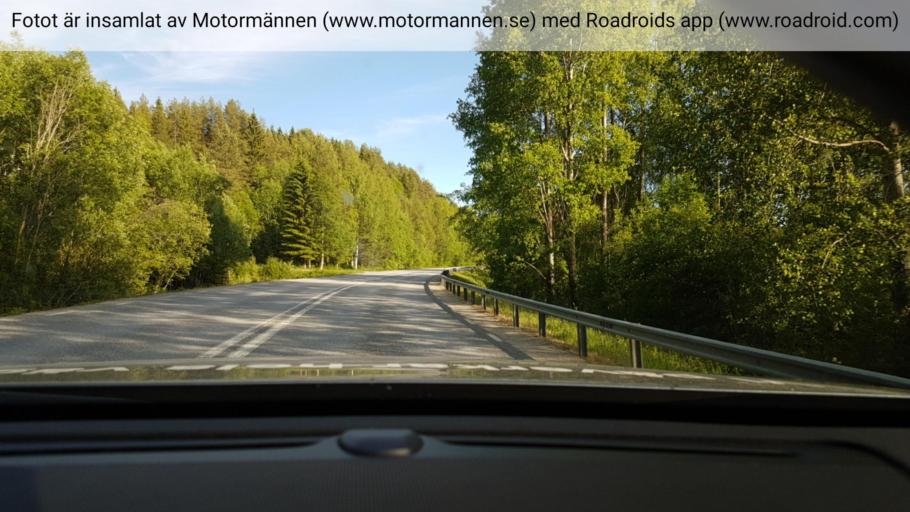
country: SE
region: Vaesterbotten
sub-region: Vindelns Kommun
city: Vindeln
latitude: 64.3114
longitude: 19.6064
